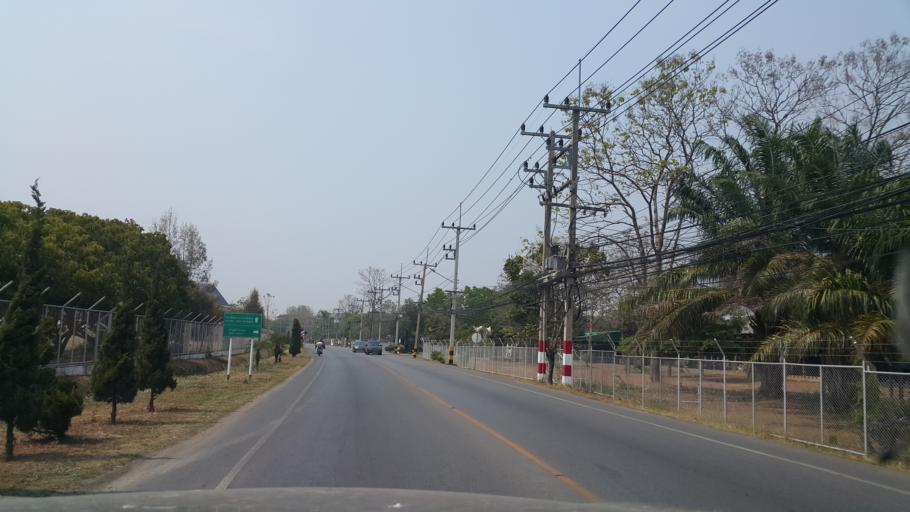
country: TH
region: Chiang Mai
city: Chiang Mai
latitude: 18.7779
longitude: 98.9670
